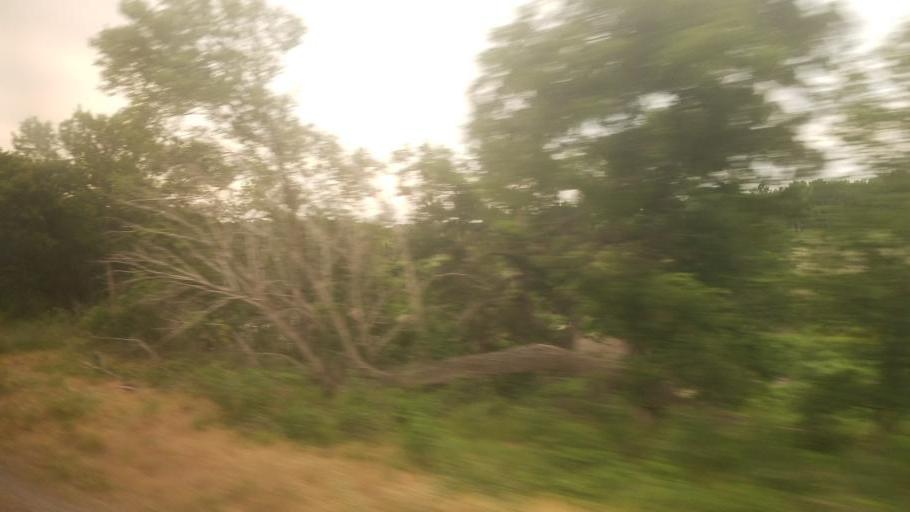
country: US
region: Kansas
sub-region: Chase County
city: Cottonwood Falls
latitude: 38.3992
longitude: -96.5548
